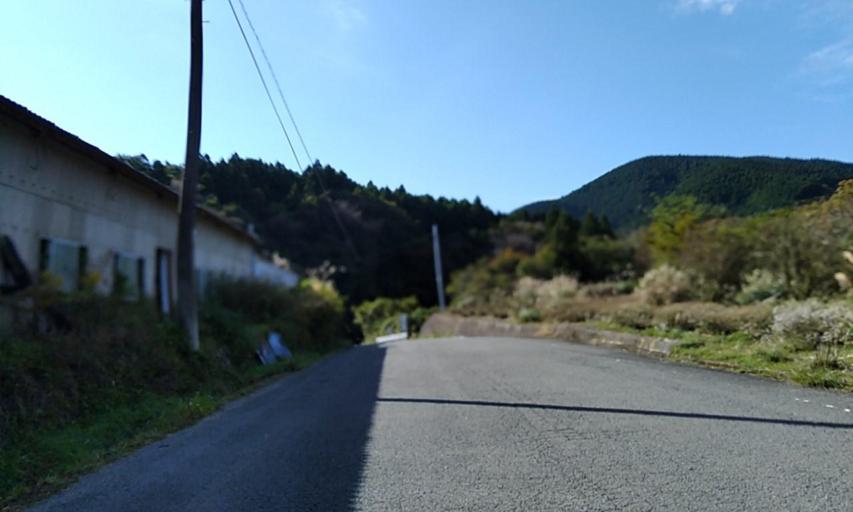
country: JP
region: Wakayama
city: Iwade
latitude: 34.1155
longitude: 135.3462
